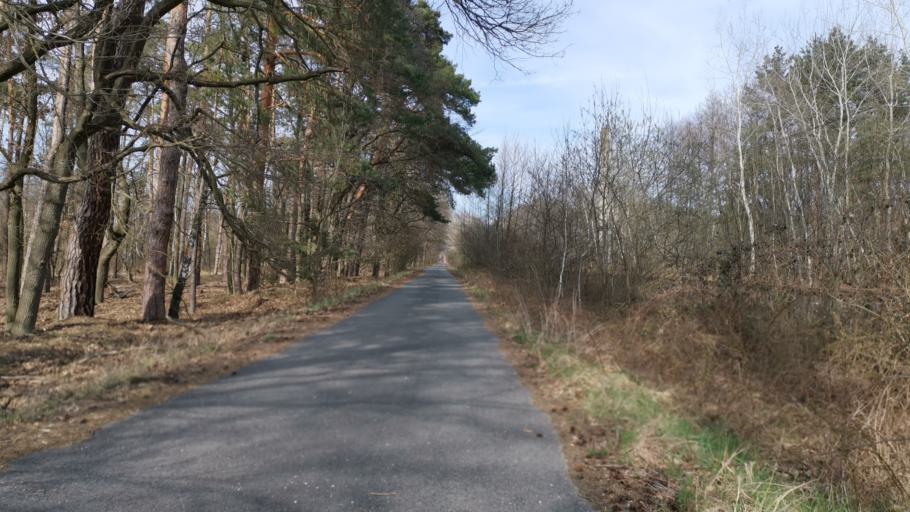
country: SK
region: Trnavsky
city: Gbely
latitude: 48.6796
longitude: 17.0600
